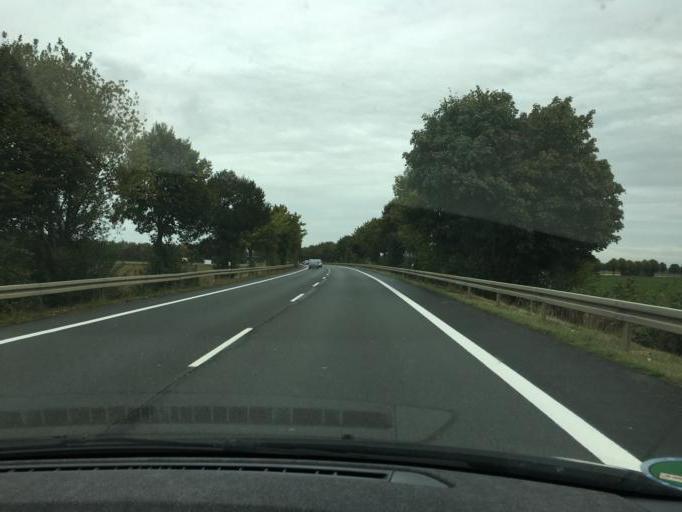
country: DE
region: North Rhine-Westphalia
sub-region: Regierungsbezirk Koln
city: Elsdorf
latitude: 50.9451
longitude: 6.5888
